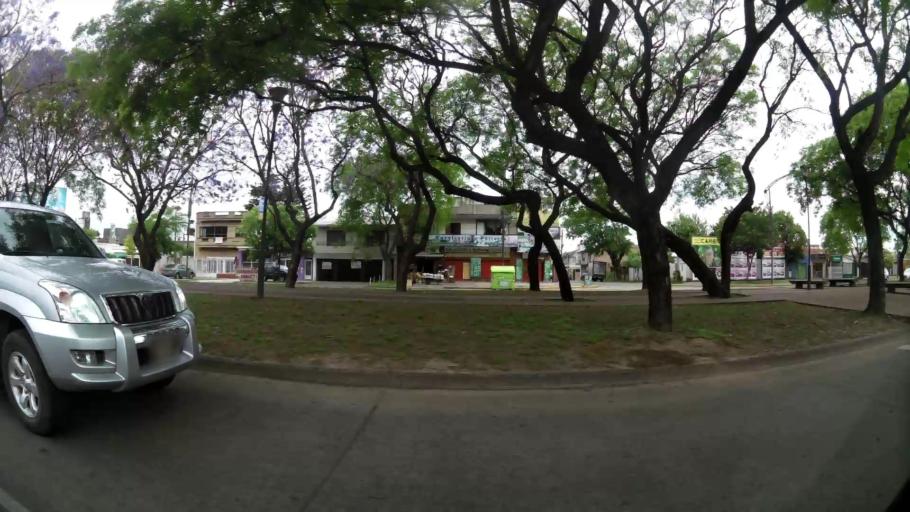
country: AR
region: Santa Fe
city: Gobernador Galvez
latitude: -33.0045
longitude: -60.6651
